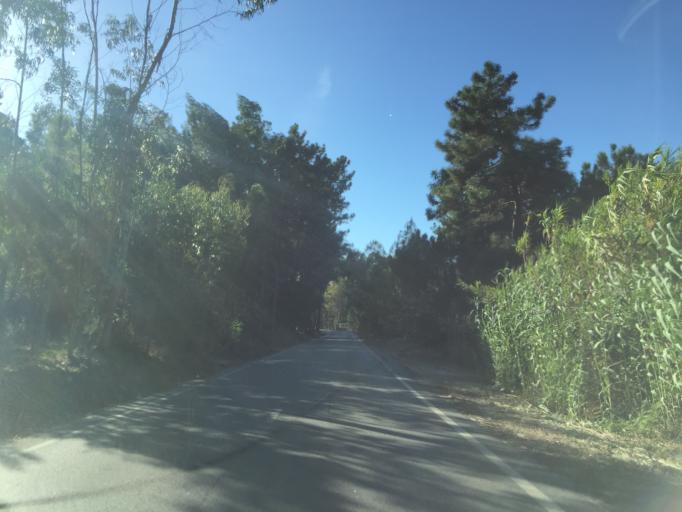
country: PT
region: Coimbra
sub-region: Figueira da Foz
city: Buarcos
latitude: 40.2157
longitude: -8.8748
